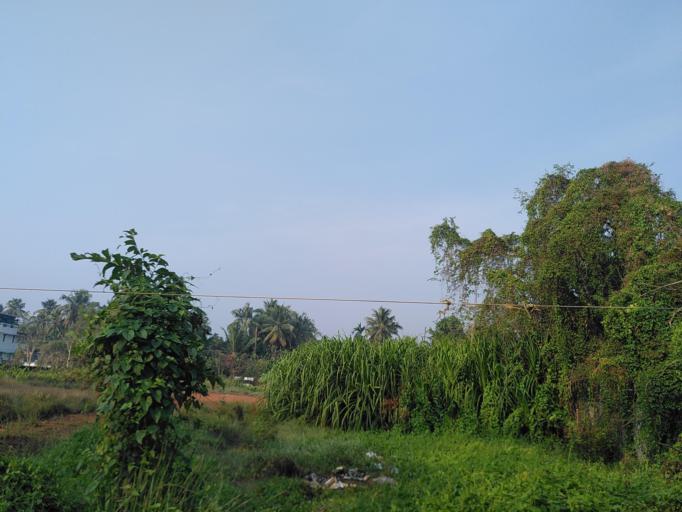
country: IN
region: Kerala
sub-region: Alappuzha
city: Arukutti
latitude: 9.9273
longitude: 76.3279
